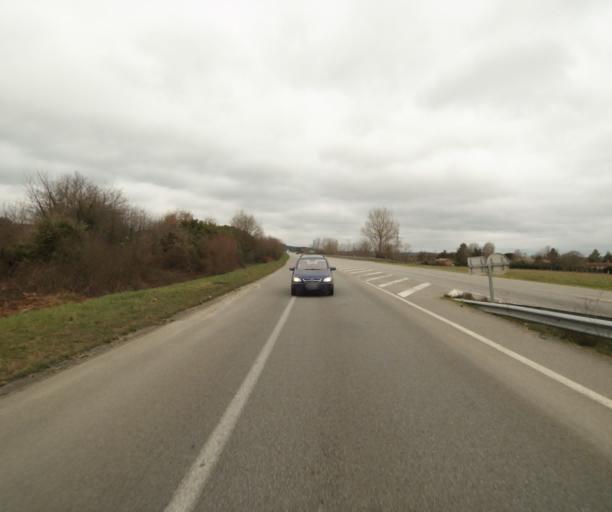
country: FR
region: Midi-Pyrenees
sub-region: Departement de l'Ariege
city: Pamiers
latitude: 43.1362
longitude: 1.6205
